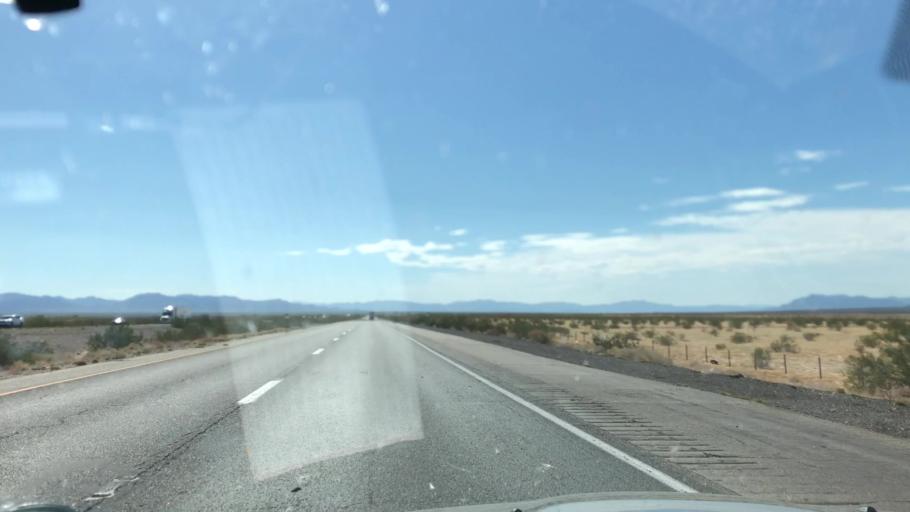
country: US
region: California
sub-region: Riverside County
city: Mesa Verde
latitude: 33.6249
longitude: -115.0504
